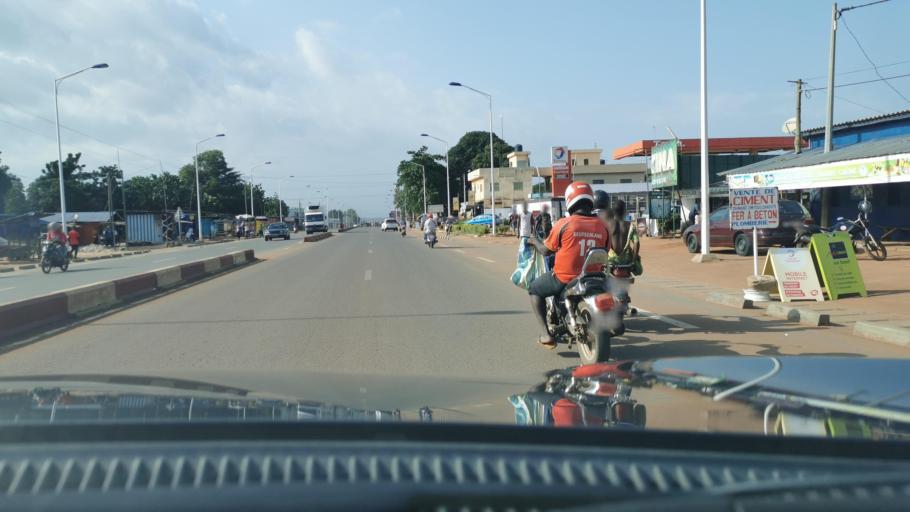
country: TG
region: Maritime
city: Lome
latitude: 6.2033
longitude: 1.2415
